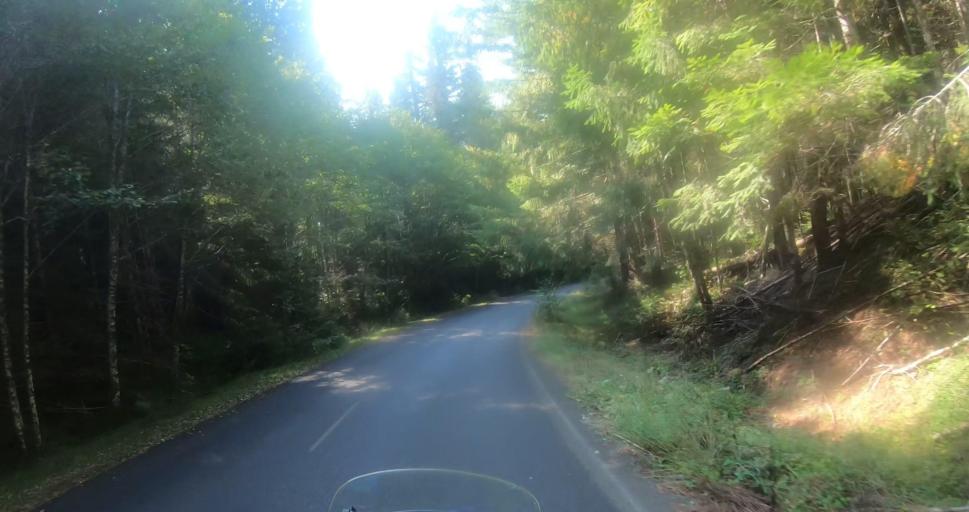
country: US
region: Washington
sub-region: Skamania County
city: Carson
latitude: 46.1790
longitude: -121.8524
